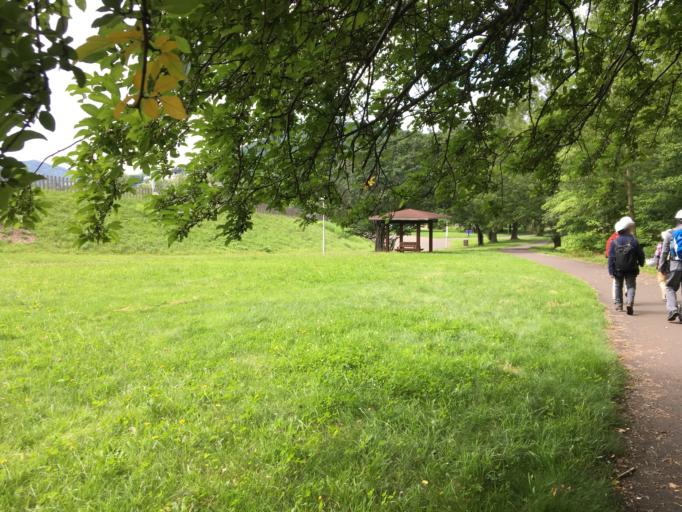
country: JP
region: Hokkaido
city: Sapporo
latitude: 42.9962
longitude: 141.3450
